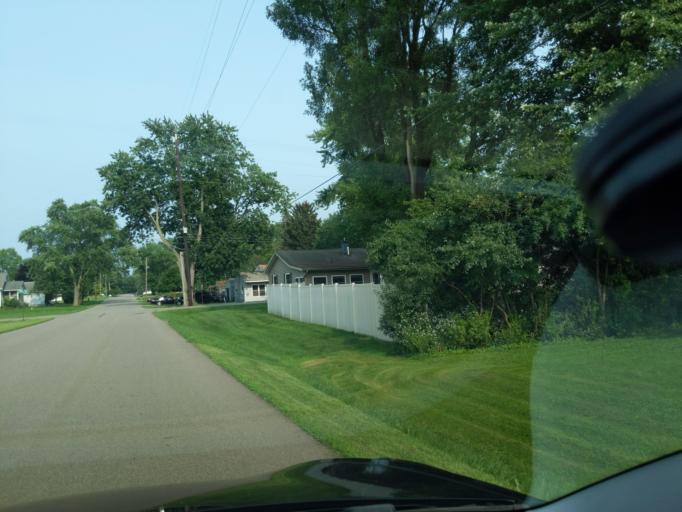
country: US
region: Michigan
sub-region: Jackson County
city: Jackson
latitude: 42.2421
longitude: -84.4376
